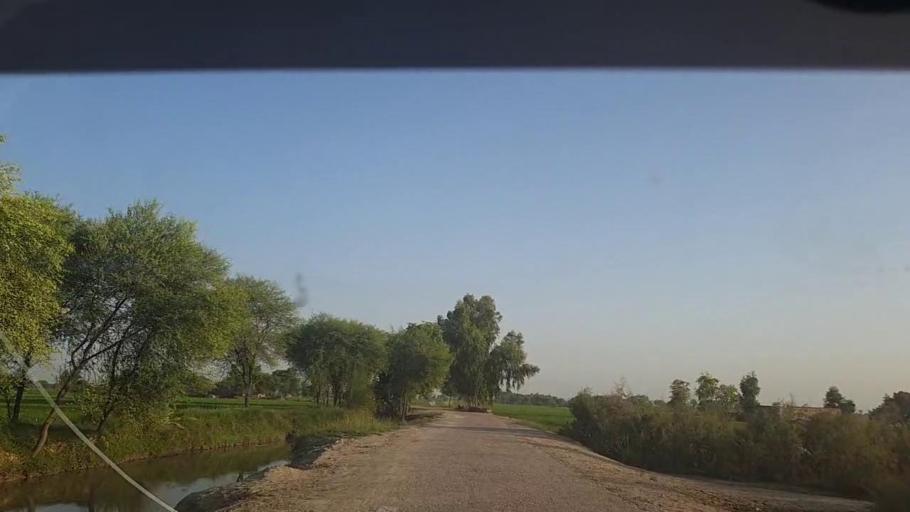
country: PK
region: Sindh
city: Thul
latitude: 28.1189
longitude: 68.8965
